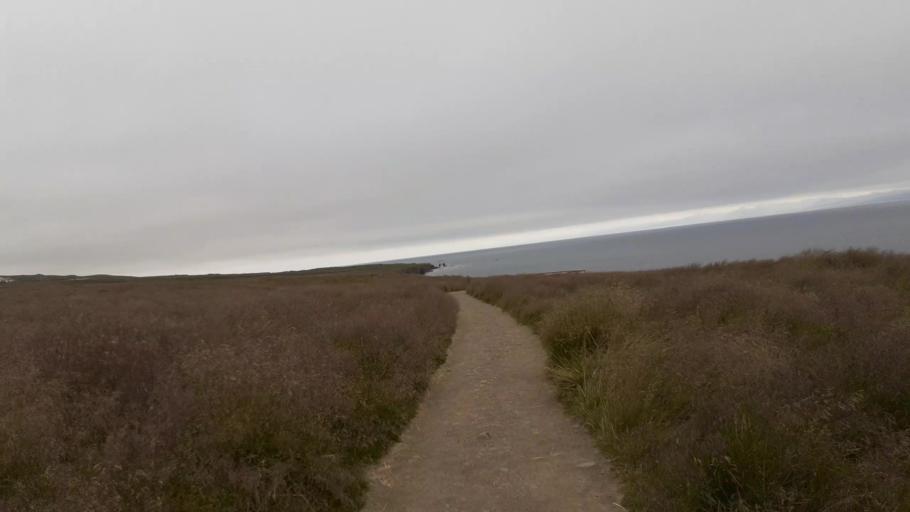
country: IS
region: Northwest
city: Saudarkrokur
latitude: 65.6049
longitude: -20.6385
